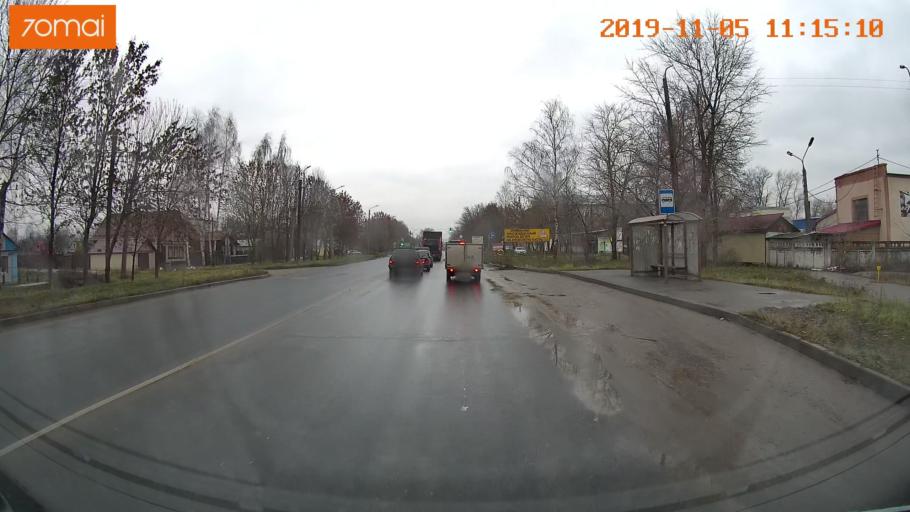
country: RU
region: Ivanovo
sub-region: Gorod Ivanovo
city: Ivanovo
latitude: 56.9767
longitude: 40.9543
